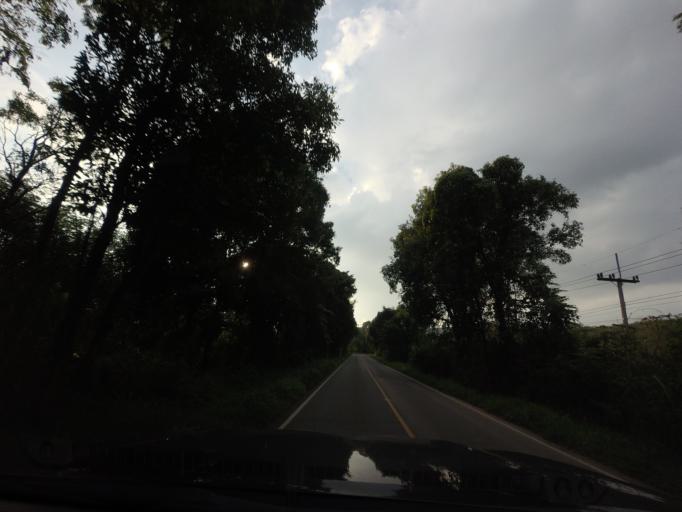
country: TH
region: Loei
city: Dan Sai
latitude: 17.3334
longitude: 101.0900
